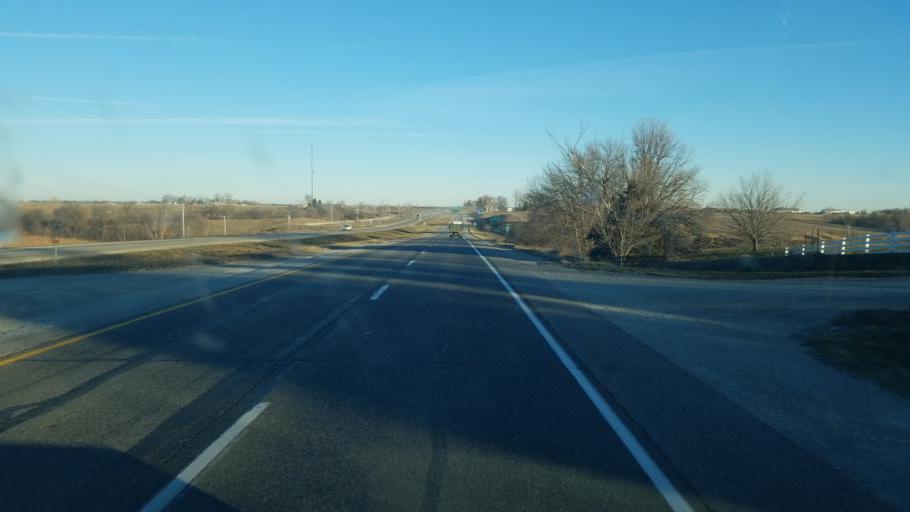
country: US
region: Iowa
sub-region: Mahaska County
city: Oskaloosa
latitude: 41.2466
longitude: -92.6406
